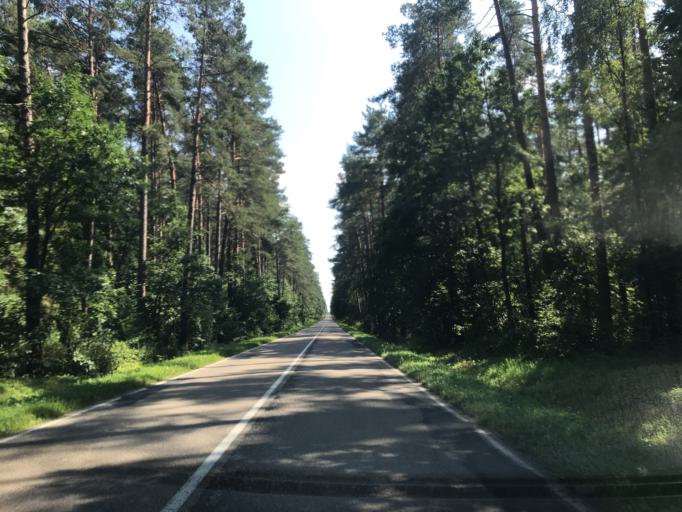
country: PL
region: Warmian-Masurian Voivodeship
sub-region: Powiat dzialdowski
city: Lidzbark
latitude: 53.2301
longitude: 19.8332
